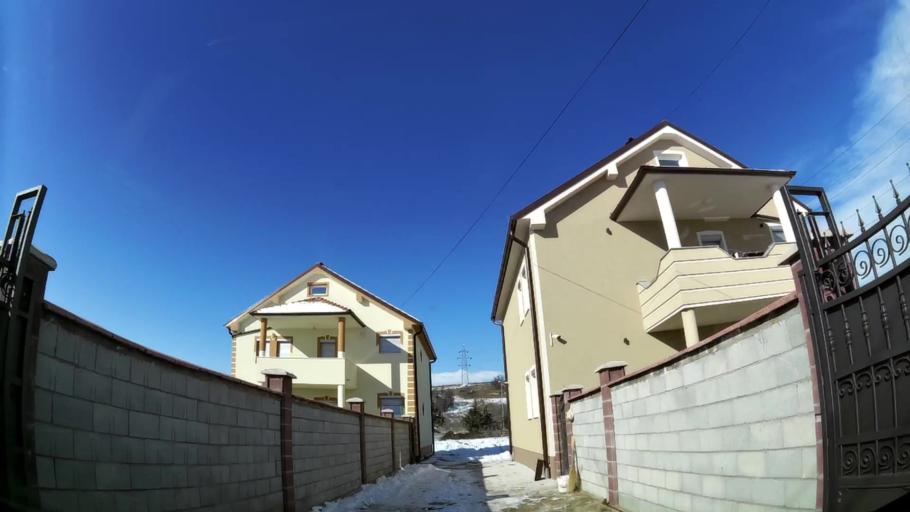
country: MK
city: Ljubin
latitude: 41.9966
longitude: 21.3177
